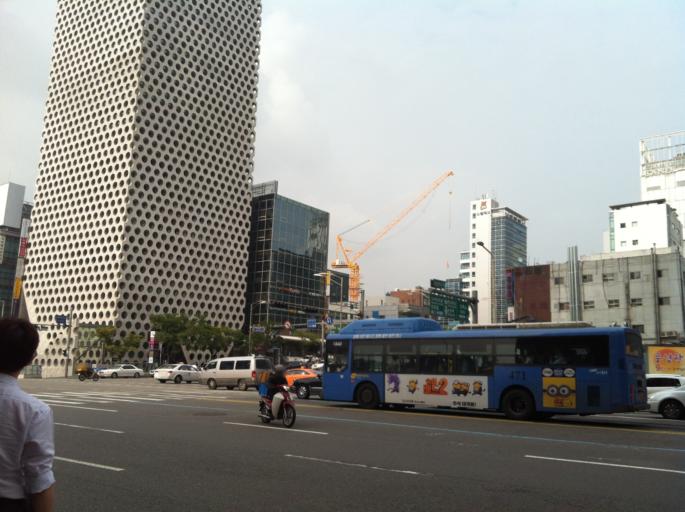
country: KR
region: Seoul
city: Seoul
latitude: 37.5043
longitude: 127.0244
